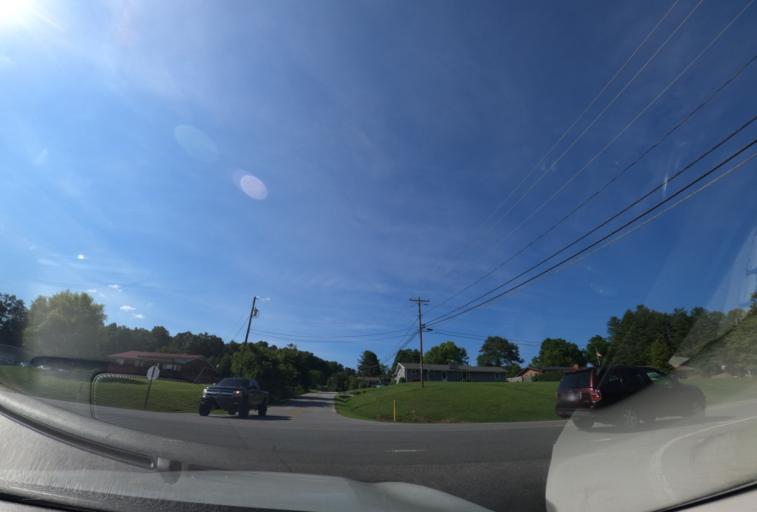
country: US
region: North Carolina
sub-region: Transylvania County
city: Brevard
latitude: 35.2702
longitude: -82.6843
